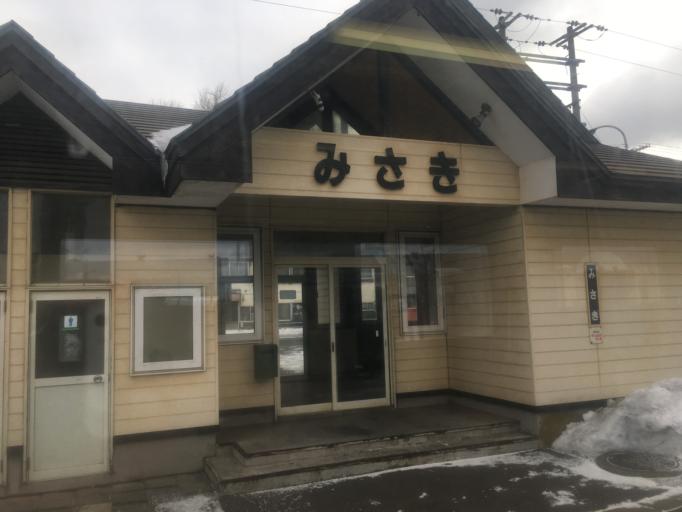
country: JP
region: Hokkaido
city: Muroran
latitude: 42.3292
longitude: 140.9938
